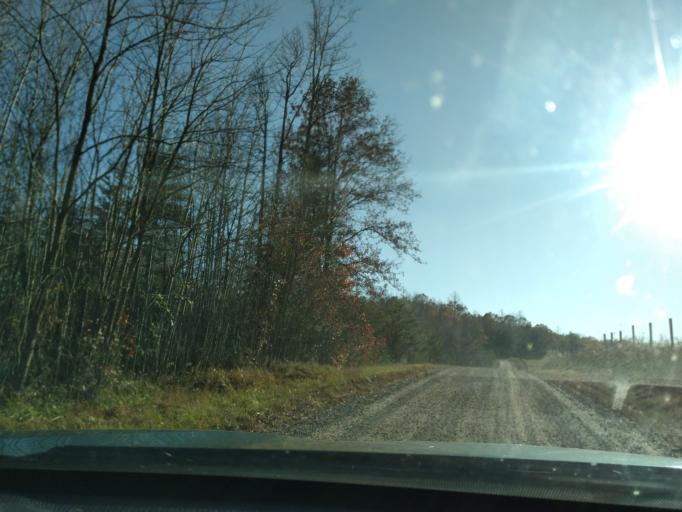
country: US
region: Virginia
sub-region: Floyd County
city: Floyd
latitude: 36.8358
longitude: -80.1957
